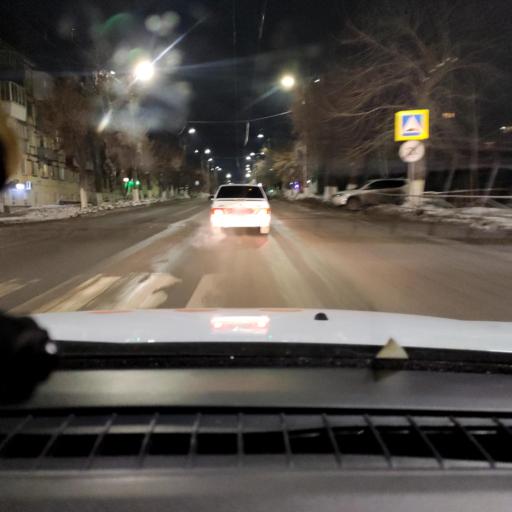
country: RU
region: Samara
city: Novokuybyshevsk
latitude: 53.0885
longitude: 49.9504
